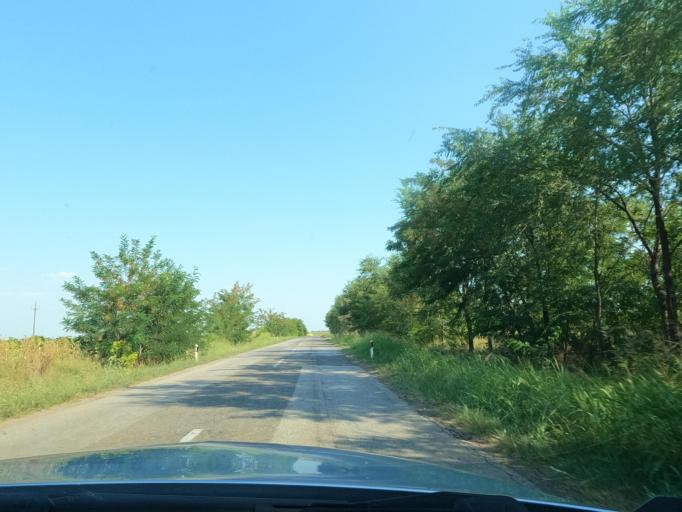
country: RS
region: Autonomna Pokrajina Vojvodina
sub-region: Juznobacki Okrug
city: Becej
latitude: 45.6598
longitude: 19.9552
